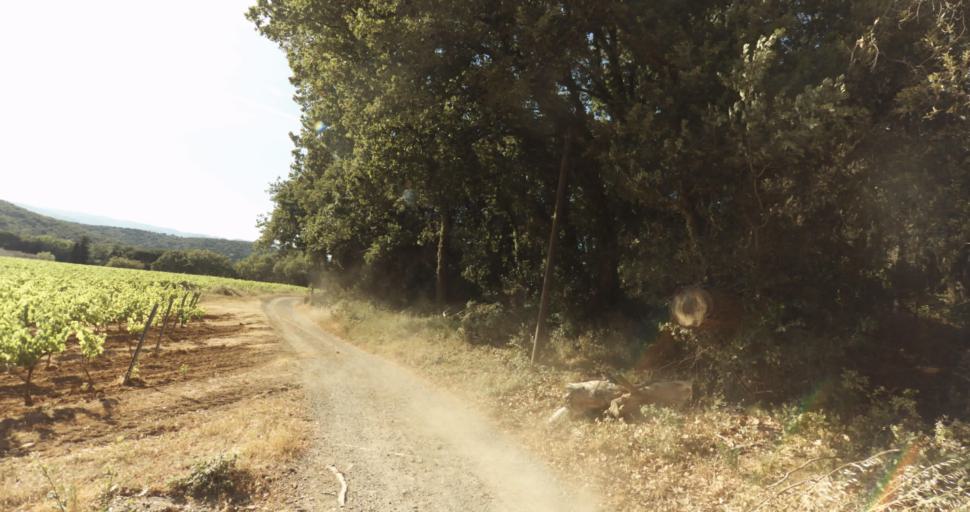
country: FR
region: Provence-Alpes-Cote d'Azur
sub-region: Departement du Var
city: Gassin
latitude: 43.2254
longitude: 6.5801
